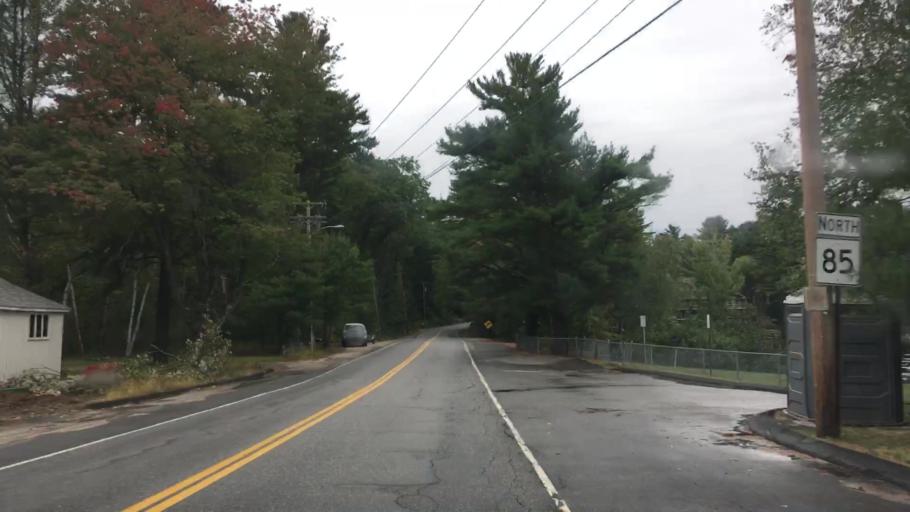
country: US
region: Maine
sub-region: Cumberland County
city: Raymond
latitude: 43.9523
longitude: -70.4641
